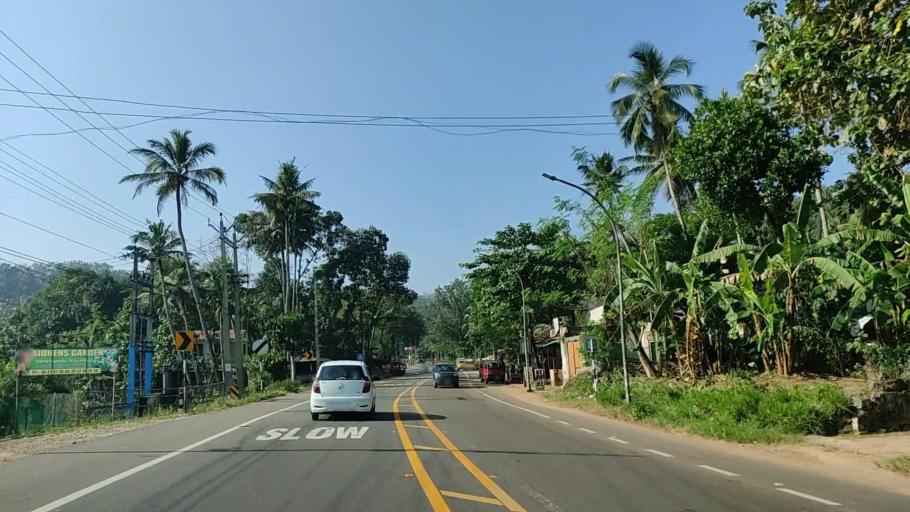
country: IN
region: Kerala
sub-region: Kollam
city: Punalur
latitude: 8.9183
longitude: 76.8550
